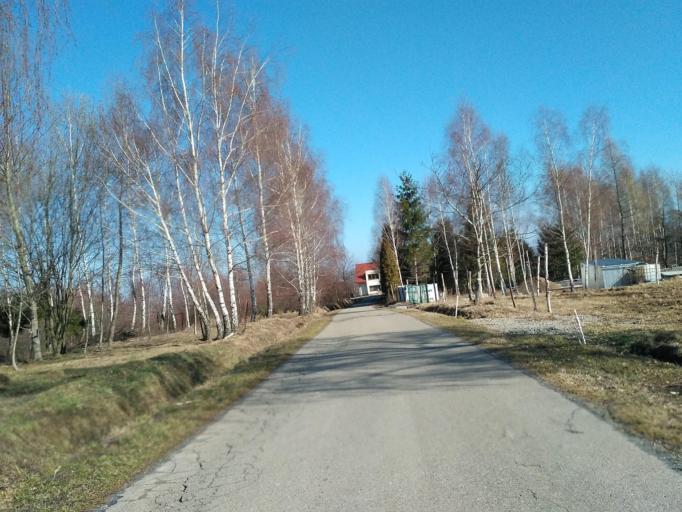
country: PL
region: Subcarpathian Voivodeship
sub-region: Powiat rzeszowski
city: Siedliska
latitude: 49.9428
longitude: 21.9513
